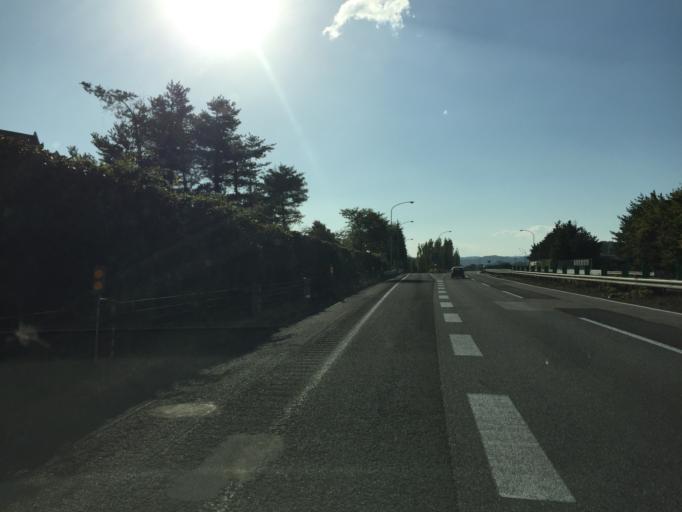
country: JP
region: Fukushima
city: Fukushima-shi
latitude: 37.7400
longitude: 140.4195
